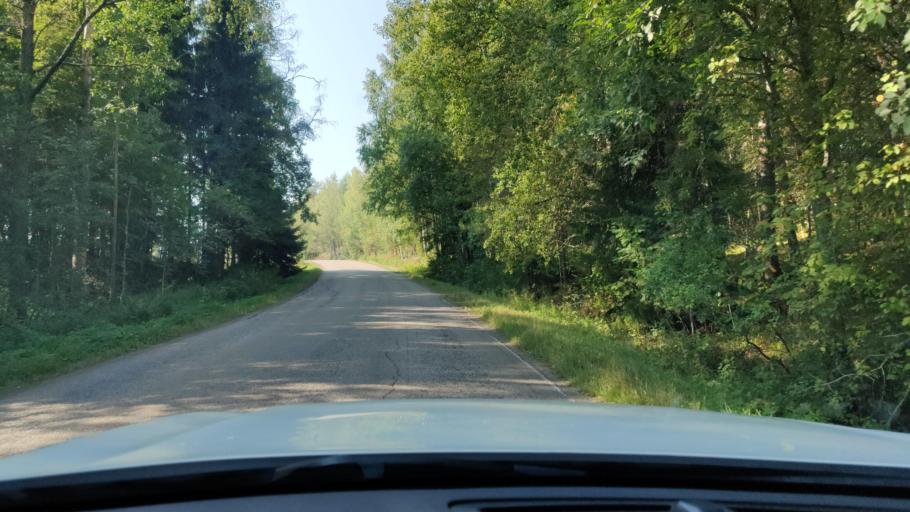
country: FI
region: Haeme
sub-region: Riihimaeki
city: Riihimaeki
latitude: 60.7129
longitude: 24.6906
